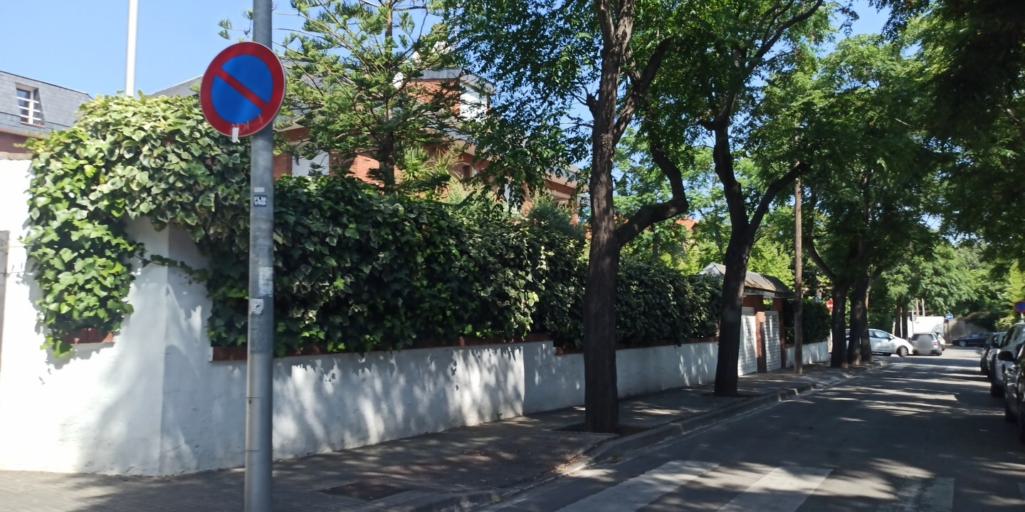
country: ES
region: Catalonia
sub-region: Provincia de Barcelona
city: Cerdanyola del Valles
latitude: 41.4879
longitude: 2.1377
